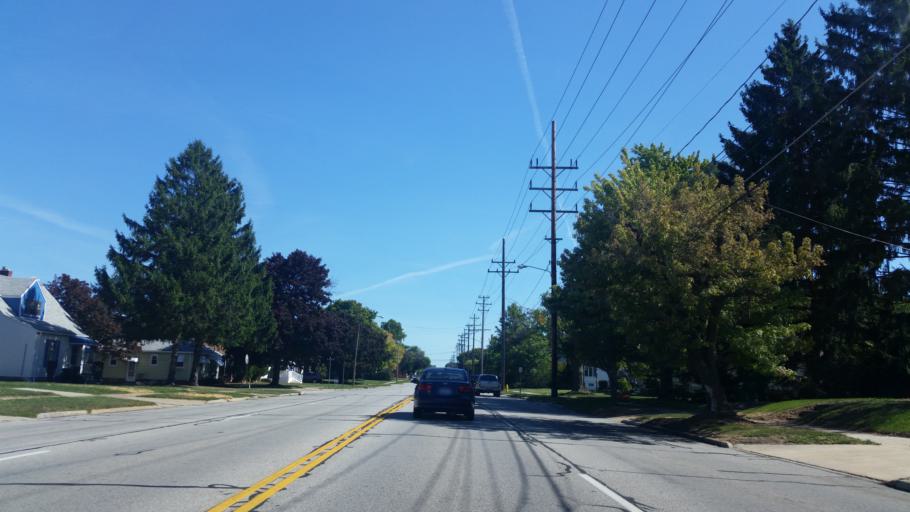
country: US
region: Ohio
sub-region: Cuyahoga County
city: Parma
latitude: 41.4049
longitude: -81.7160
